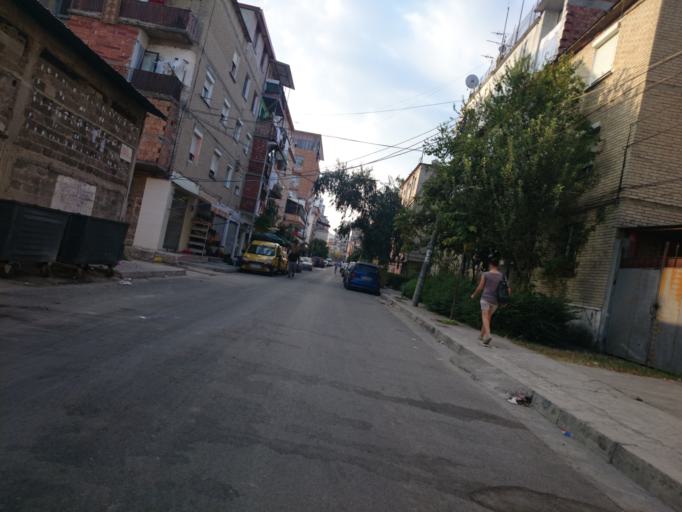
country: AL
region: Tirane
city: Tirana
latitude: 41.3268
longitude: 19.7935
